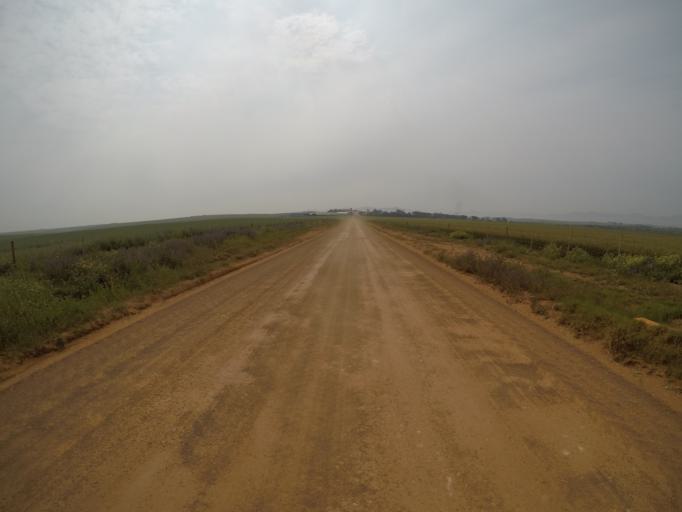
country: ZA
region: Western Cape
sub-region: City of Cape Town
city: Kraaifontein
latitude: -33.7123
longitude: 18.6859
